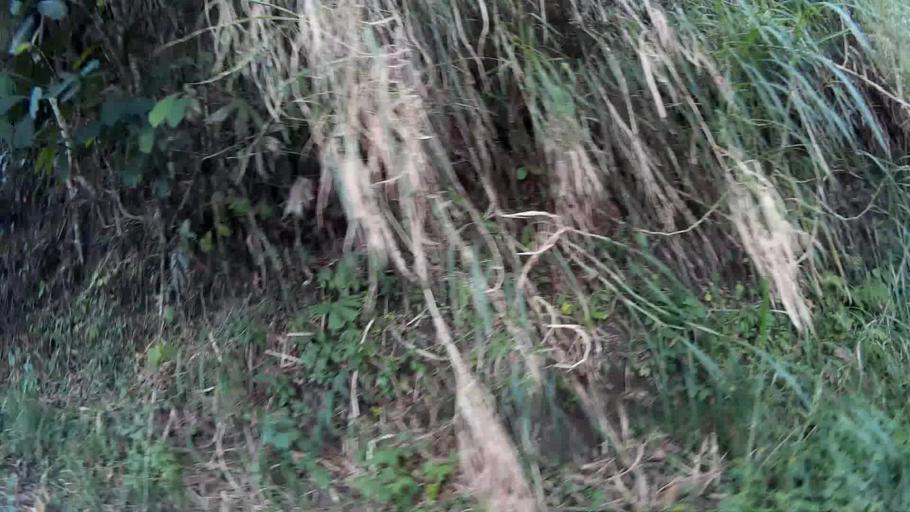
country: CO
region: Valle del Cauca
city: Ulloa
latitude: 4.7141
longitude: -75.7179
